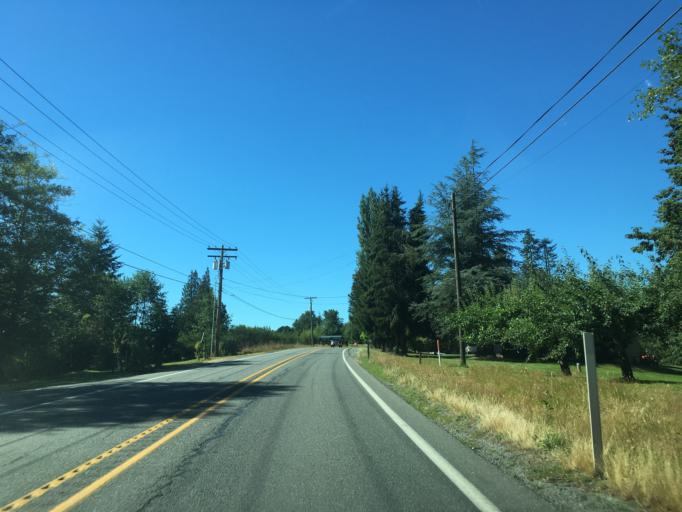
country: US
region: Washington
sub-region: Skagit County
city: Big Lake
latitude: 48.4120
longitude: -122.2479
